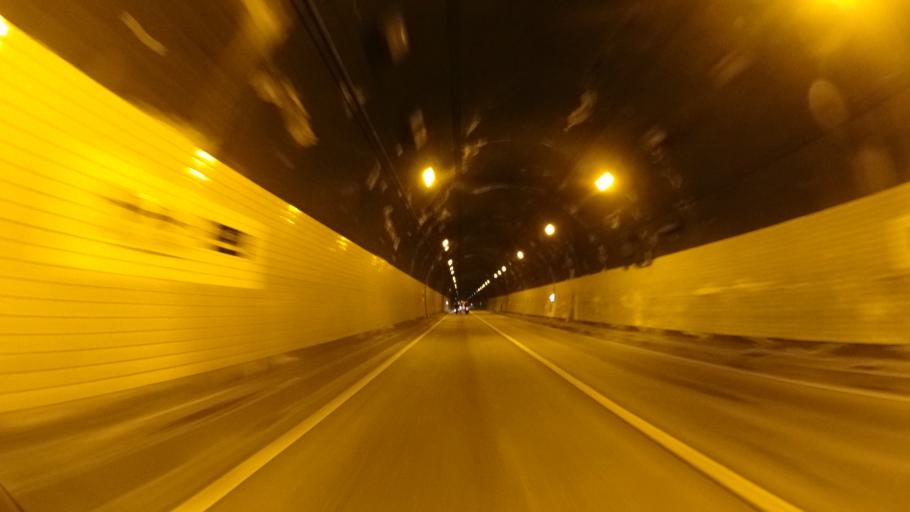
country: JP
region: Ehime
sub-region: Nishiuwa-gun
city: Ikata-cho
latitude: 33.4909
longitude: 132.3850
